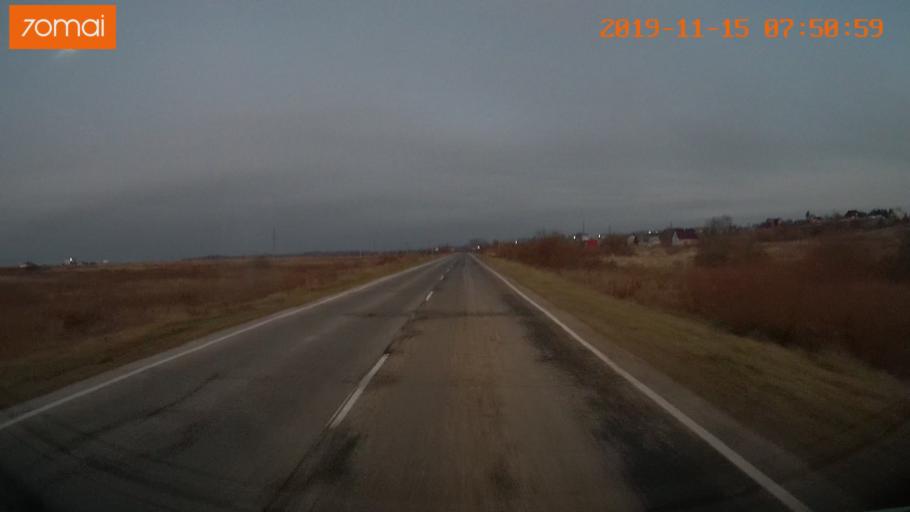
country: RU
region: Vologda
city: Cherepovets
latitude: 58.8743
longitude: 38.2114
